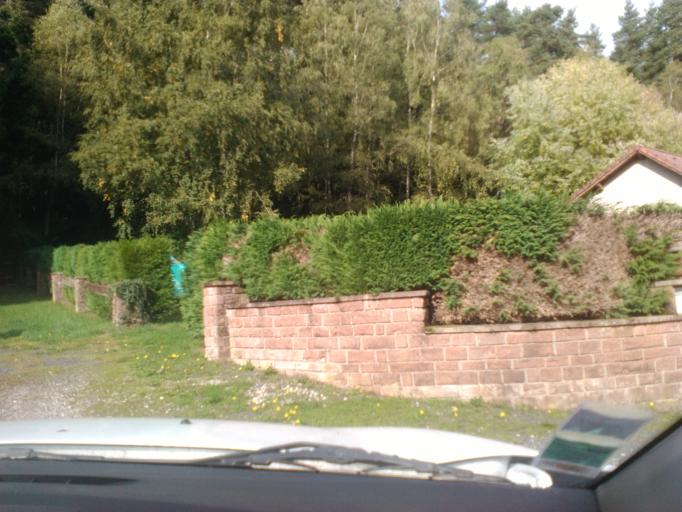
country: FR
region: Lorraine
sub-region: Departement des Vosges
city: Saint-Michel-sur-Meurthe
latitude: 48.3139
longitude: 6.8540
